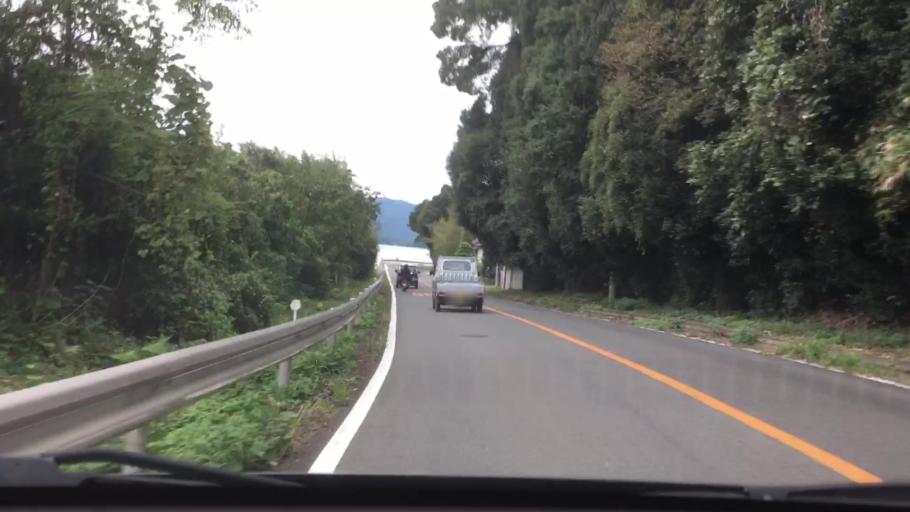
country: JP
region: Nagasaki
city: Sasebo
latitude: 33.0310
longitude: 129.7435
